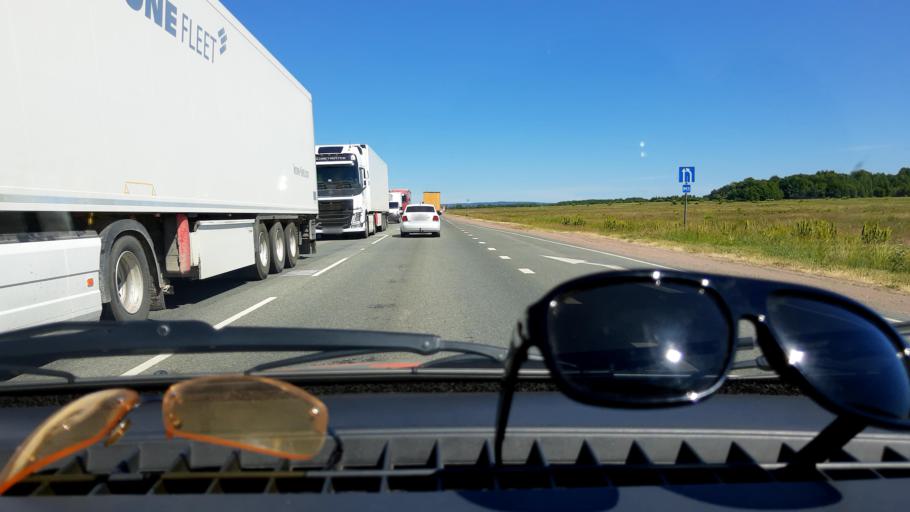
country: RU
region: Bashkortostan
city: Kudeyevskiy
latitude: 54.8170
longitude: 56.7983
